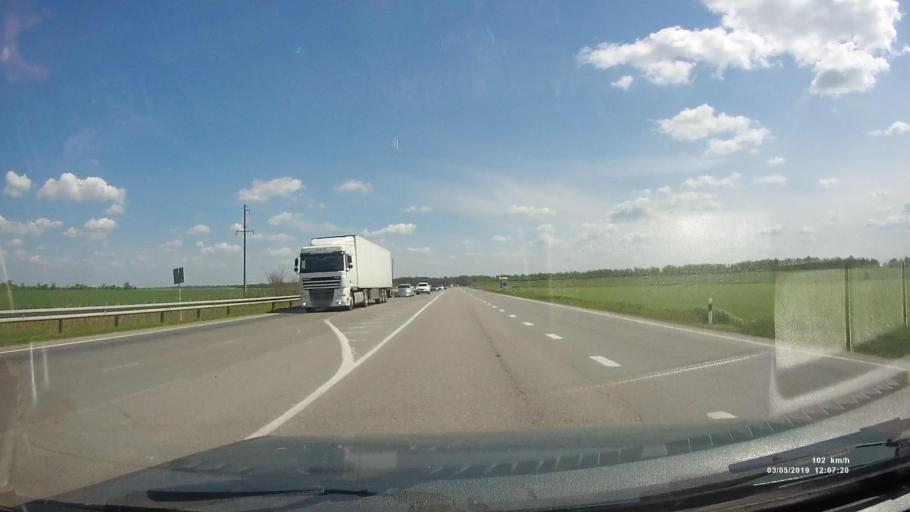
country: RU
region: Rostov
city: Bagayevskaya
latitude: 47.2848
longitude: 40.4726
